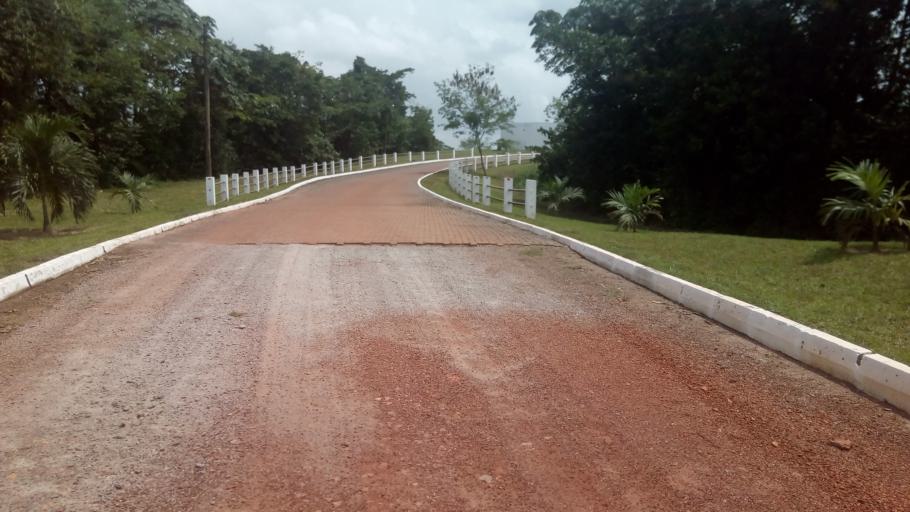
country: GH
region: Western
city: Tarkwa
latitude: 5.2990
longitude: -2.0120
